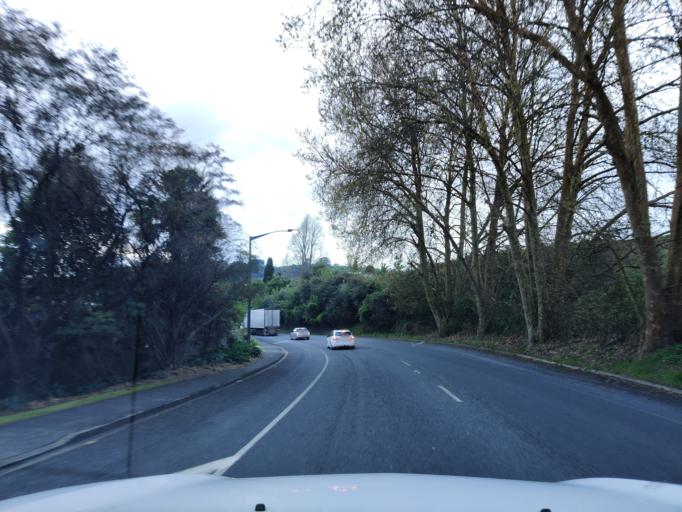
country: NZ
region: Waikato
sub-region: Otorohanga District
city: Otorohanga
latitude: -38.3405
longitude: 175.1671
